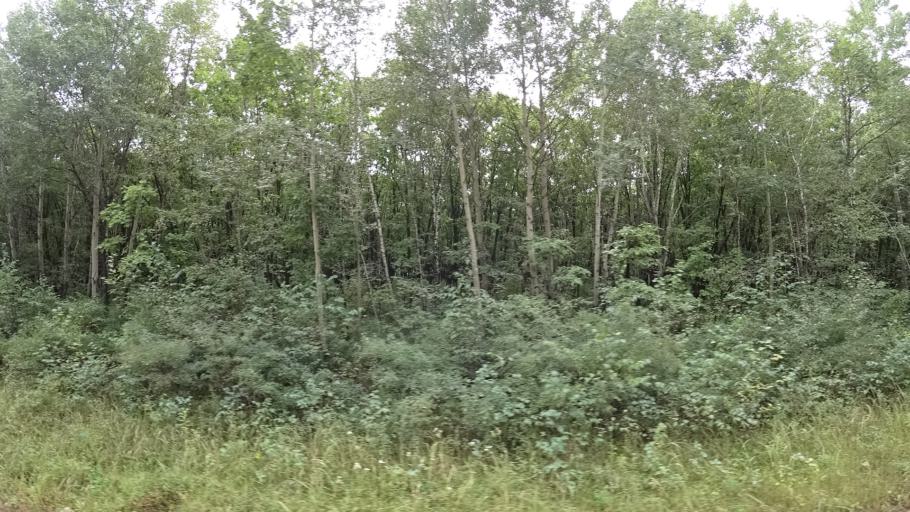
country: RU
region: Primorskiy
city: Lyalichi
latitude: 44.0860
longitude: 132.4401
